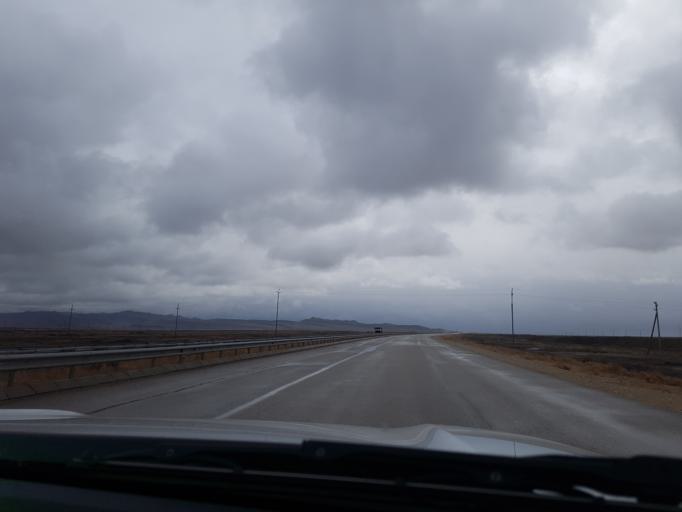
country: TM
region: Balkan
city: Balkanabat
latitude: 39.8194
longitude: 54.1472
